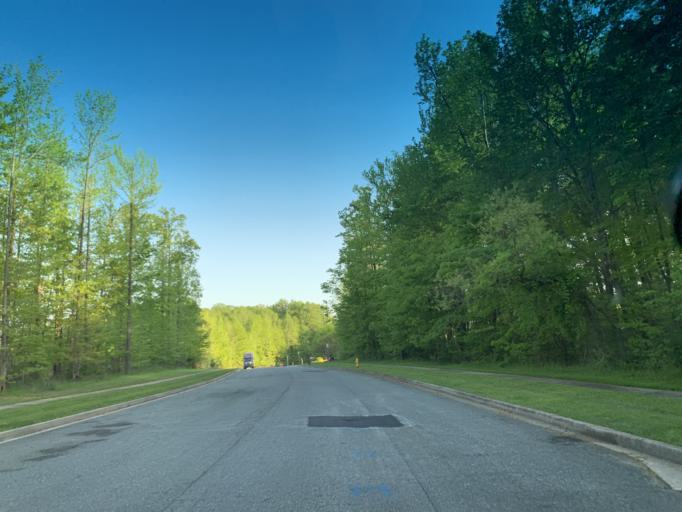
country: US
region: Maryland
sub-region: Harford County
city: Aberdeen
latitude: 39.5273
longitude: -76.1985
